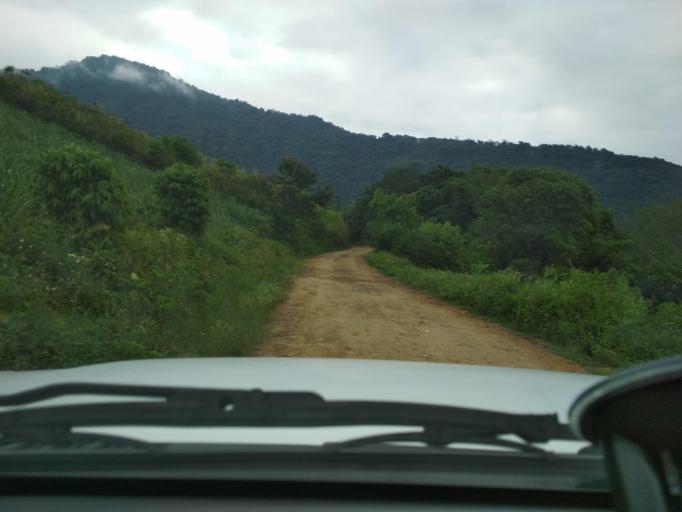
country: MX
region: Veracruz
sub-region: Fortin
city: Monte Salas
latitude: 18.9227
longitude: -97.0391
